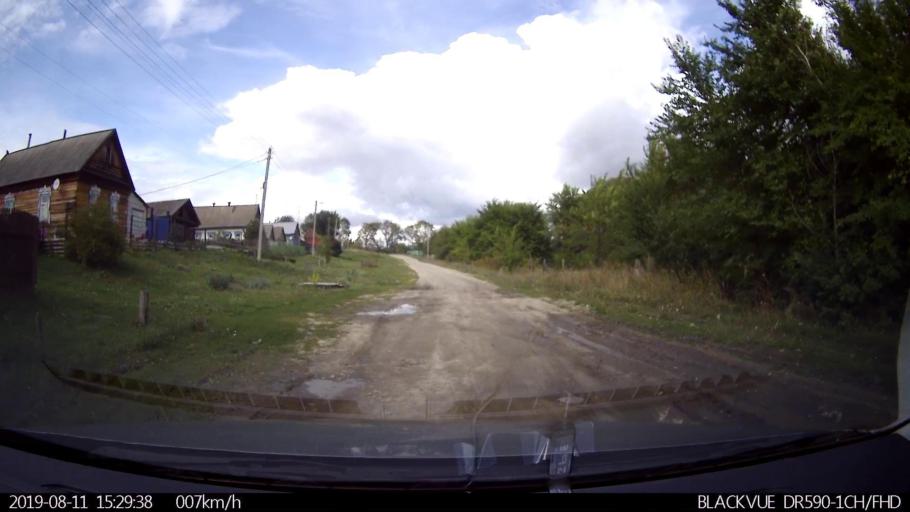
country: RU
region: Ulyanovsk
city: Ignatovka
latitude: 53.8542
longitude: 47.5744
